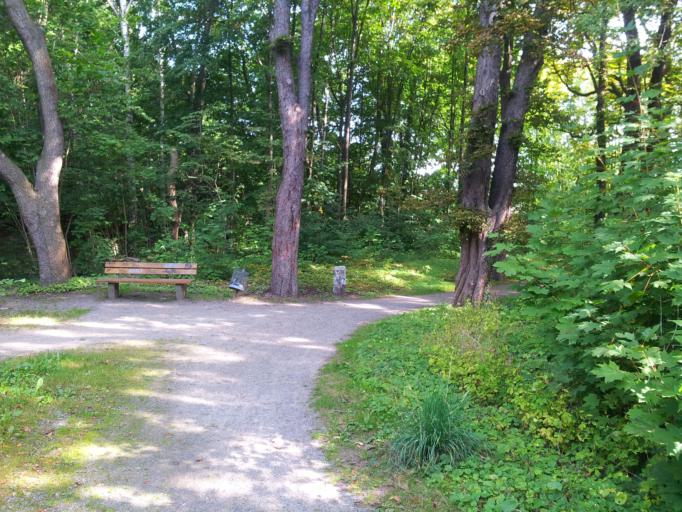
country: DE
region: Lower Saxony
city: Goslar
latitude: 51.9114
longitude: 10.4431
